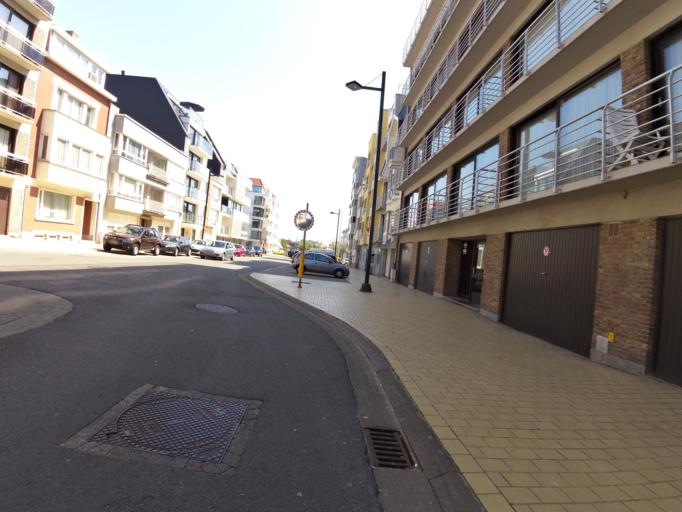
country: BE
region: Flanders
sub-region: Provincie West-Vlaanderen
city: Middelkerke
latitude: 51.1866
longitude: 2.8138
